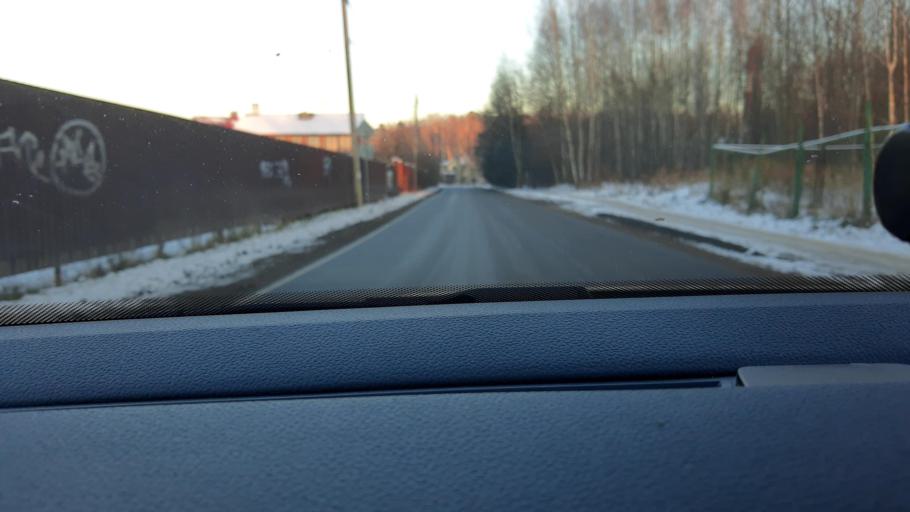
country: RU
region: Moskovskaya
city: Pirogovskiy
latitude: 55.9639
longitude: 37.7352
